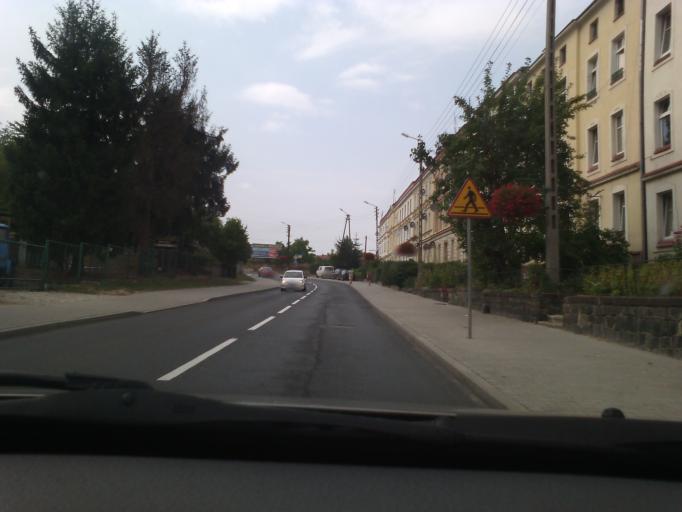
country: PL
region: Lower Silesian Voivodeship
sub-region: Powiat swidnicki
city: Swiebodzice
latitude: 50.8612
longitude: 16.3122
